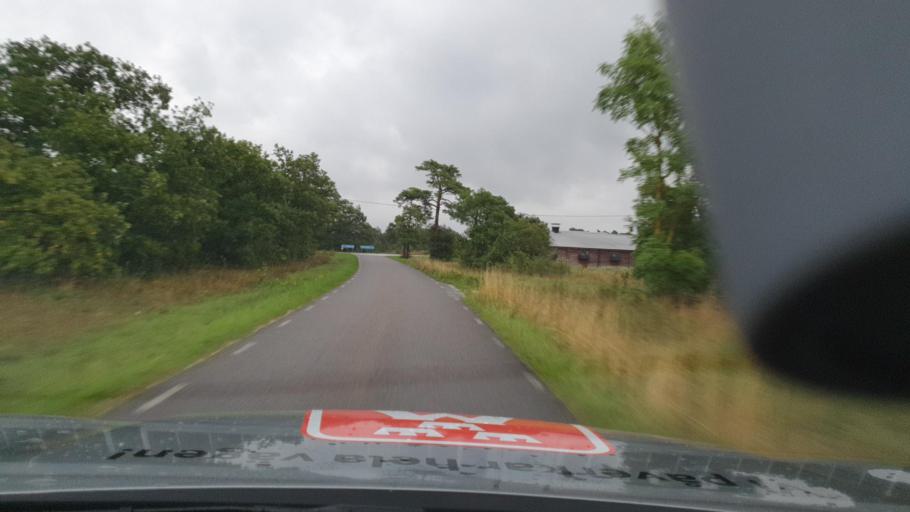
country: SE
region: Gotland
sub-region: Gotland
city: Slite
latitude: 57.8054
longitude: 18.6292
